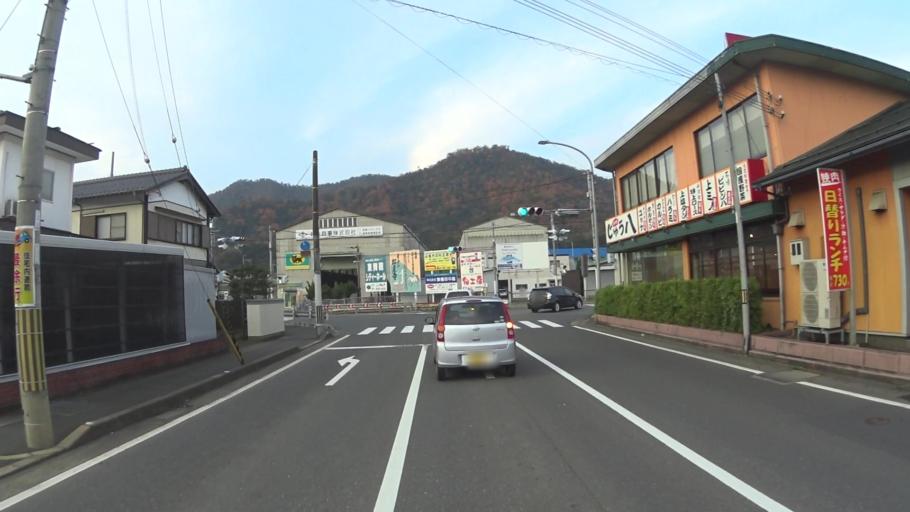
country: JP
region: Kyoto
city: Maizuru
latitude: 35.4803
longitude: 135.4255
